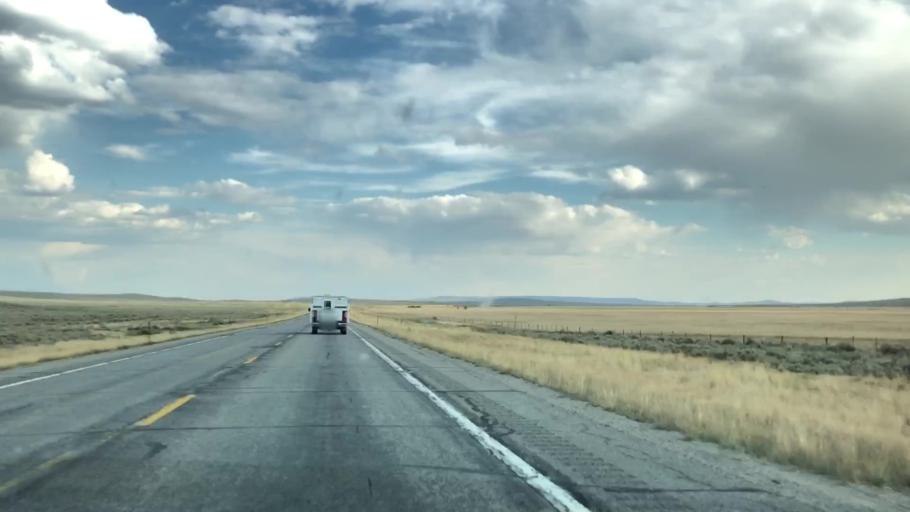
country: US
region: Wyoming
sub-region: Sublette County
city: Pinedale
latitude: 43.0443
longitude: -110.1445
